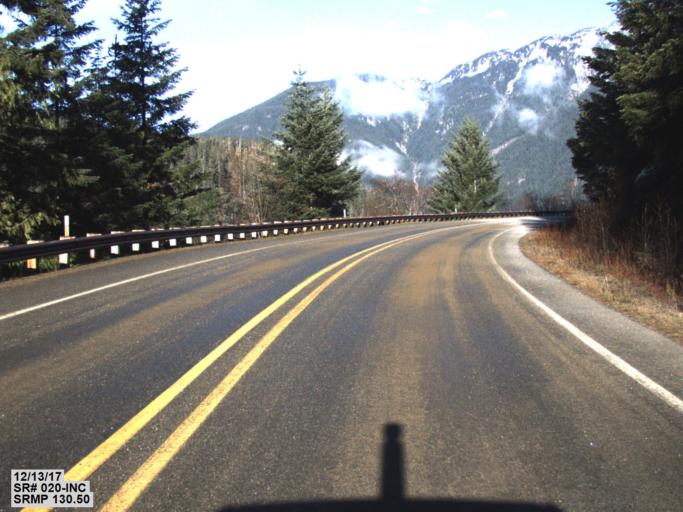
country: US
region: Washington
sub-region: Snohomish County
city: Darrington
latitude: 48.6928
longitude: -121.0951
